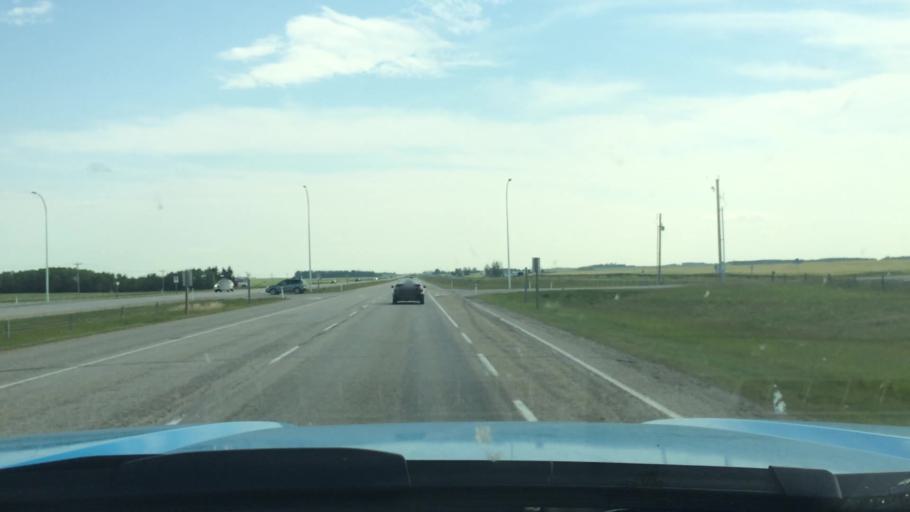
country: CA
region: Alberta
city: Olds
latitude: 51.8540
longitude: -114.0256
